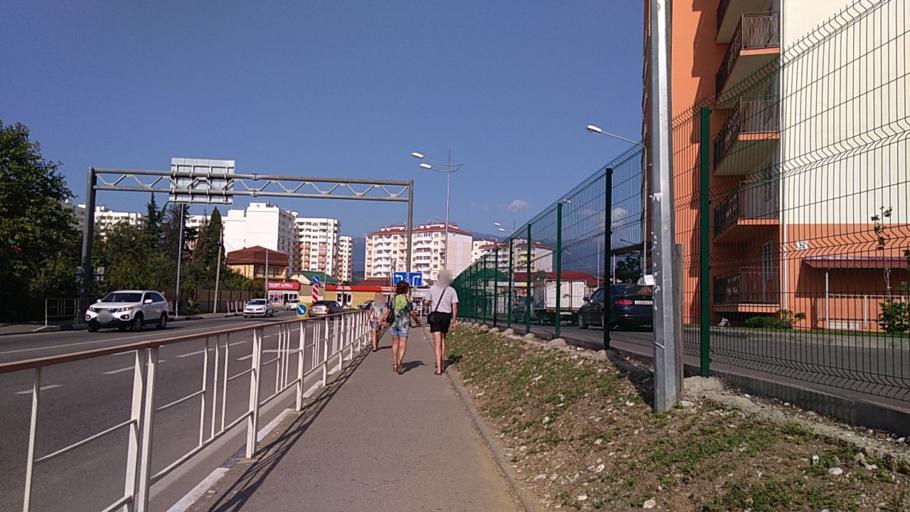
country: RU
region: Krasnodarskiy
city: Vysokoye
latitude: 43.4016
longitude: 40.0009
